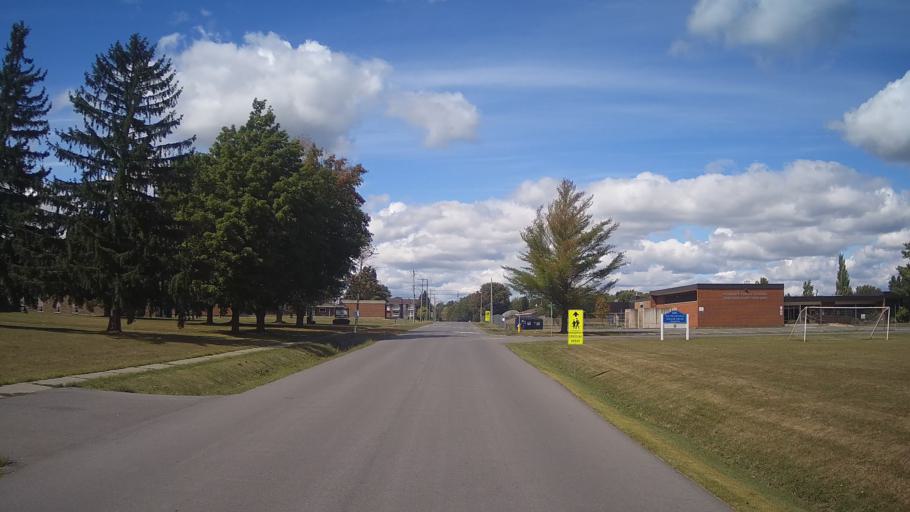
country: US
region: New York
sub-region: St. Lawrence County
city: Ogdensburg
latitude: 44.8480
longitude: -75.3131
